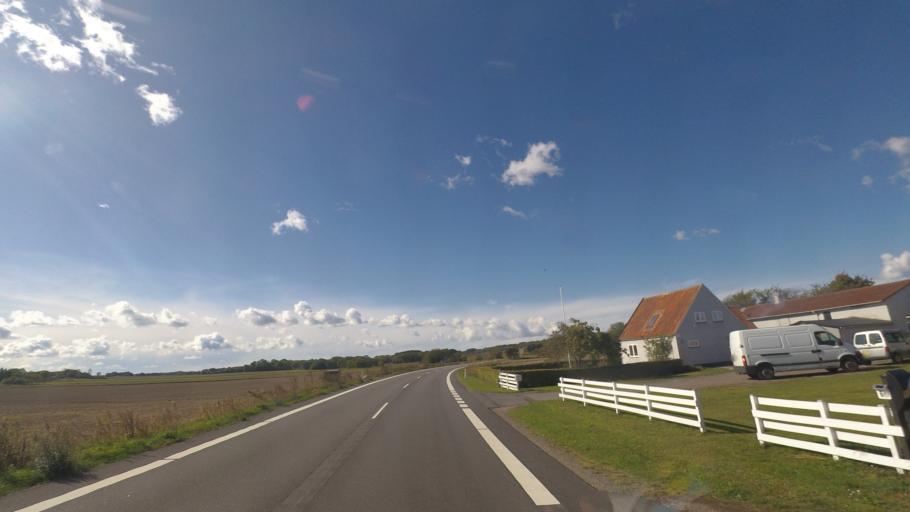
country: DK
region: Capital Region
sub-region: Bornholm Kommune
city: Nexo
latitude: 55.0607
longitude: 15.0494
